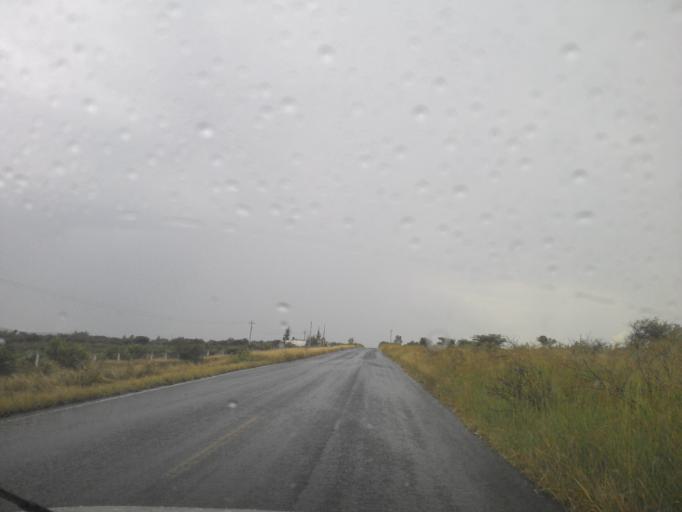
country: MX
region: Jalisco
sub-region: Arandas
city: Santiaguito (Santiaguito de Velazquez)
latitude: 20.8260
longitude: -102.1359
